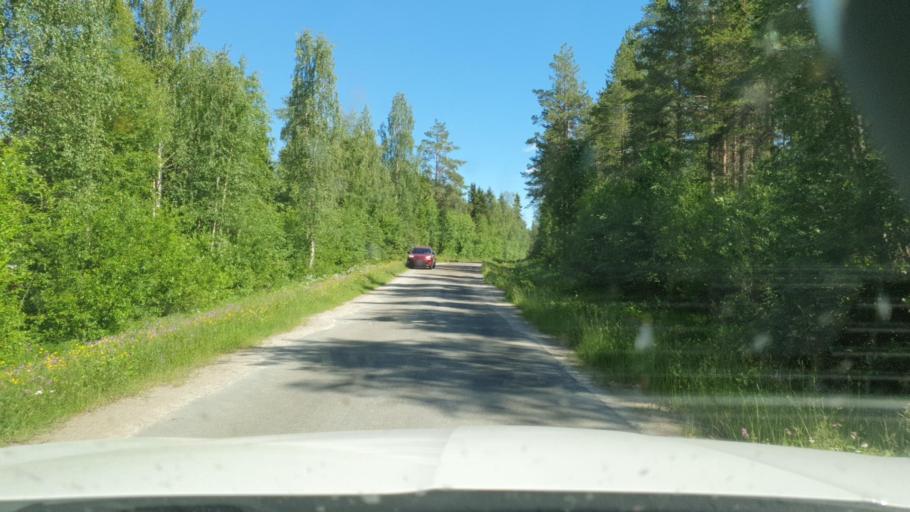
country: SE
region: Vaesterbotten
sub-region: Skelleftea Kommun
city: Byske
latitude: 65.1060
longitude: 21.1784
